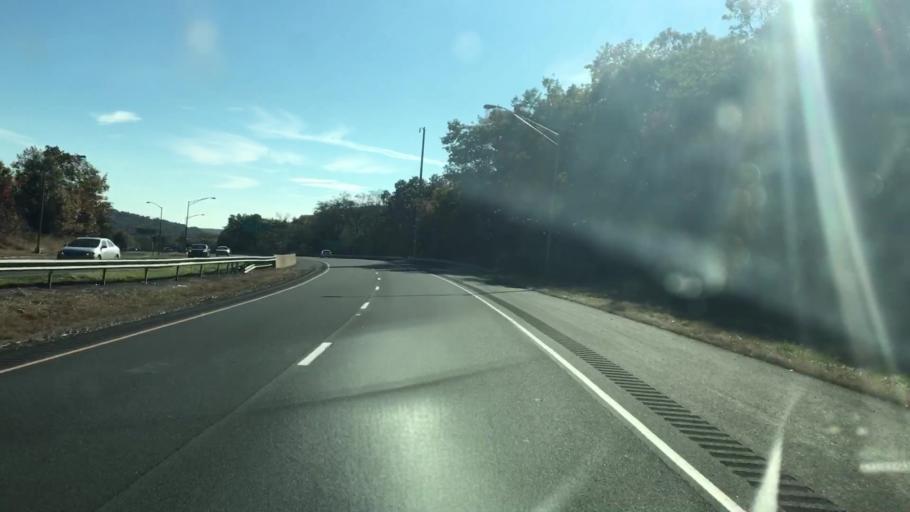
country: US
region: Connecticut
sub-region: New Haven County
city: Naugatuck
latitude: 41.5170
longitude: -73.0495
